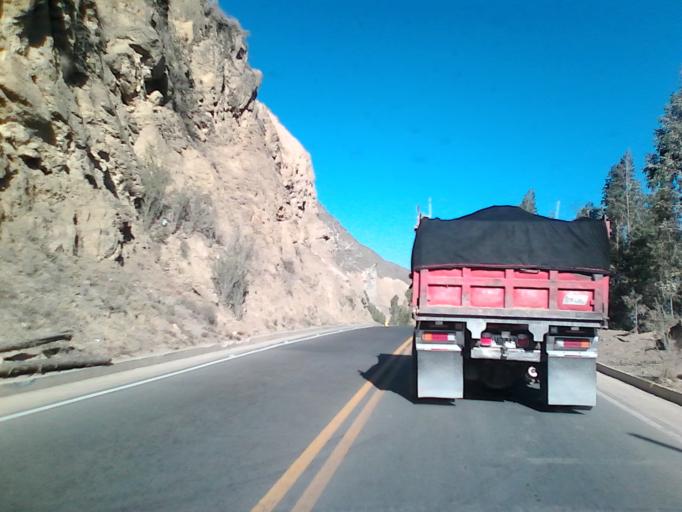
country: CO
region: Boyaca
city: Cucaita
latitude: 5.5518
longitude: -73.4916
